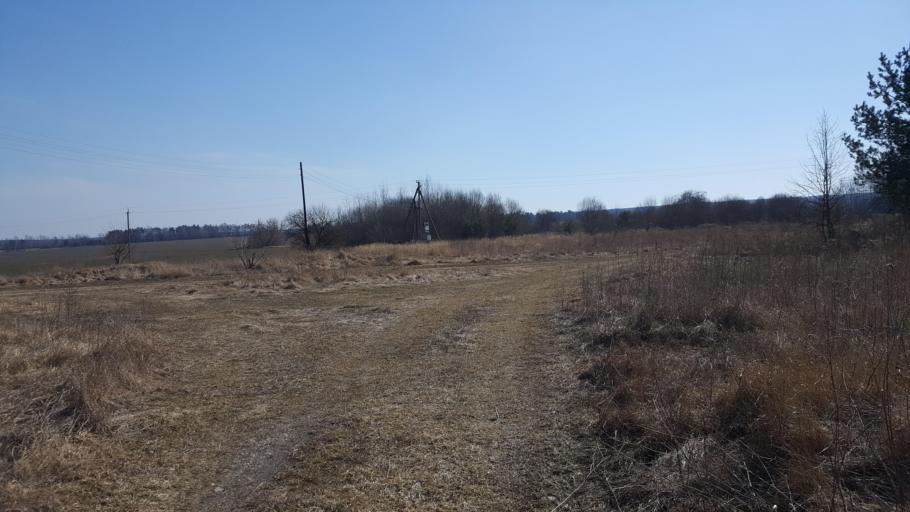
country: BY
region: Brest
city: Kamyanyets
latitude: 52.3725
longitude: 23.7763
